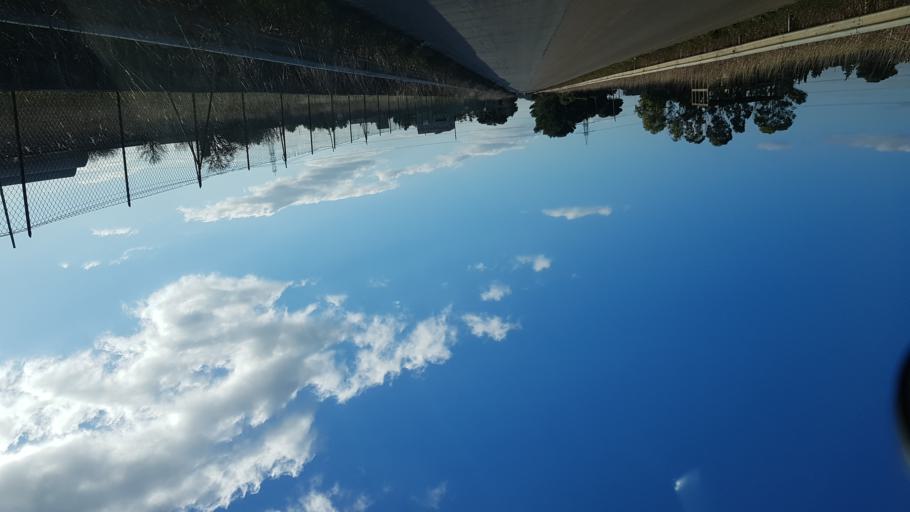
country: IT
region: Apulia
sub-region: Provincia di Brindisi
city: La Rosa
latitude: 40.6001
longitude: 17.9573
